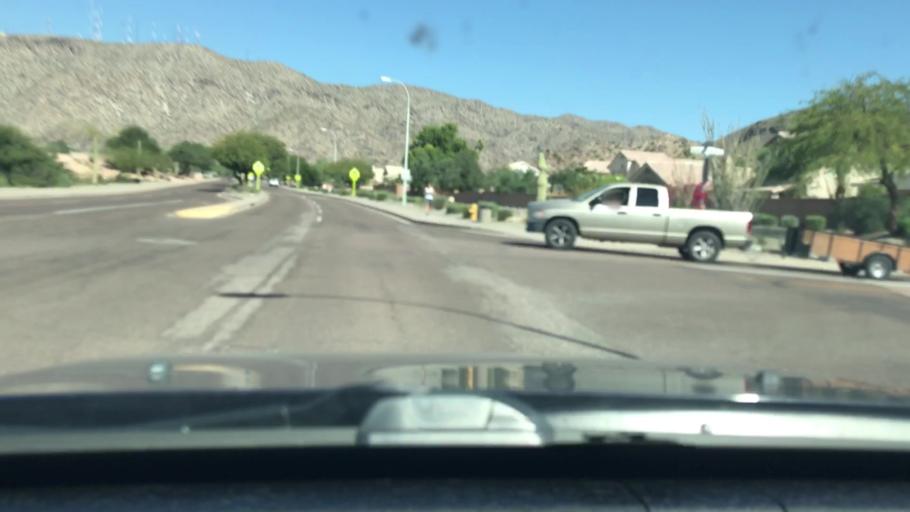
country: US
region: Arizona
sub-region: Maricopa County
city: Guadalupe
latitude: 33.3092
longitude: -112.0548
